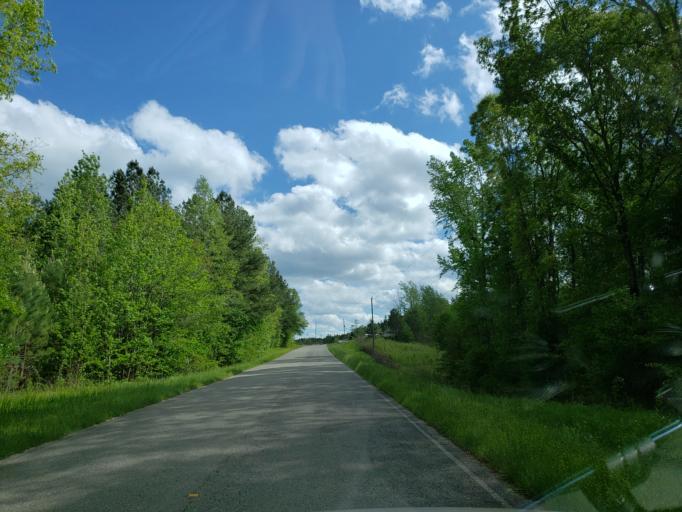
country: US
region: Georgia
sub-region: Haralson County
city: Tallapoosa
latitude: 33.7245
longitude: -85.3909
